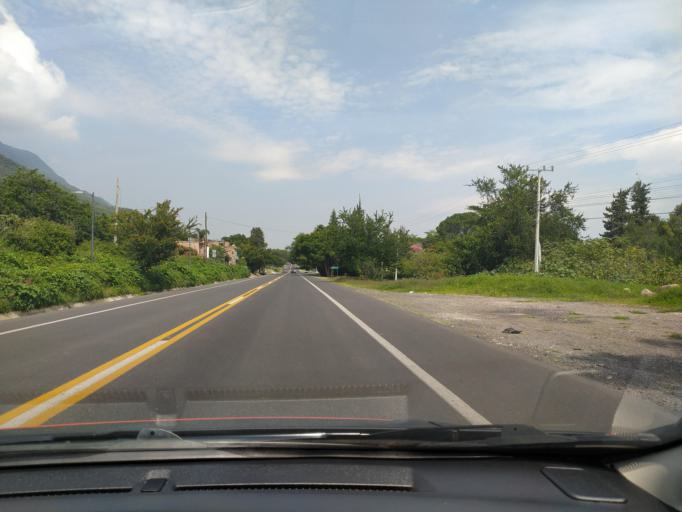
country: MX
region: Jalisco
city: San Juan Cosala
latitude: 20.2938
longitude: -103.3803
